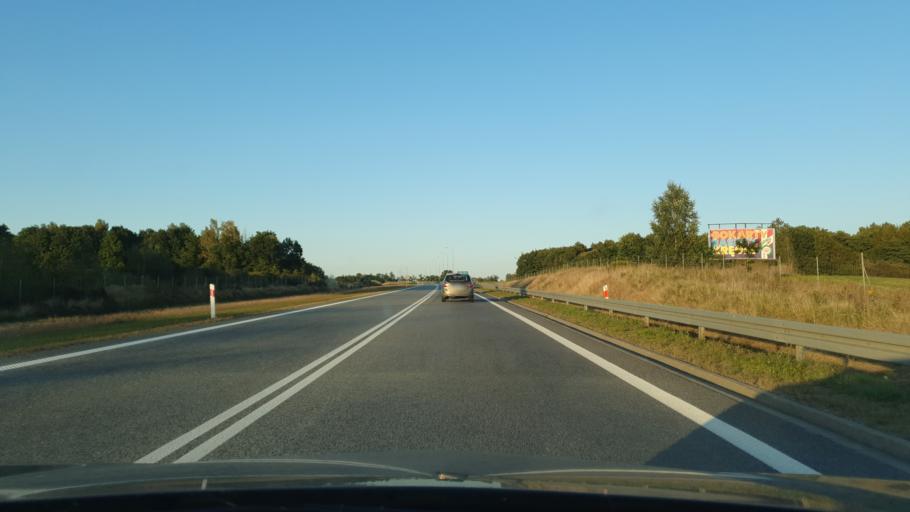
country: PL
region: Pomeranian Voivodeship
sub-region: Slupsk
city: Slupsk
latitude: 54.4627
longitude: 17.1089
